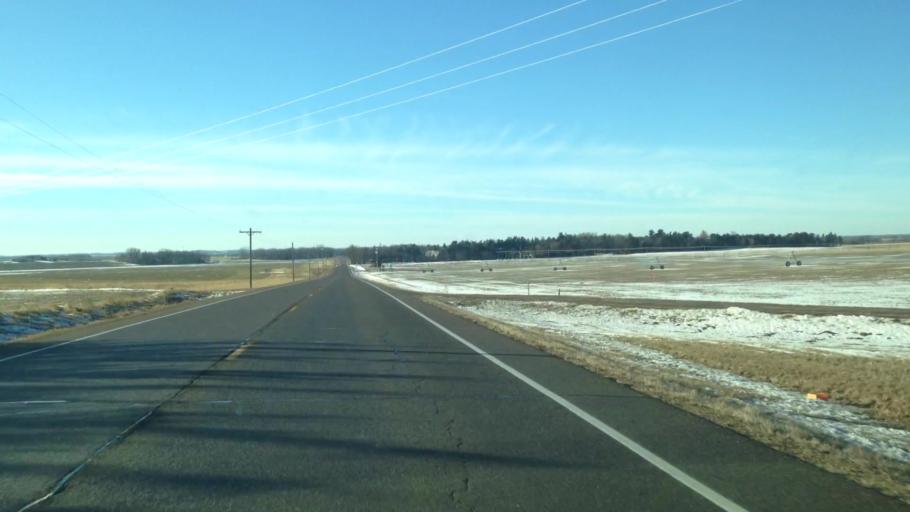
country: US
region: Minnesota
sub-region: Dakota County
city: Farmington
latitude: 44.5562
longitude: -93.0449
